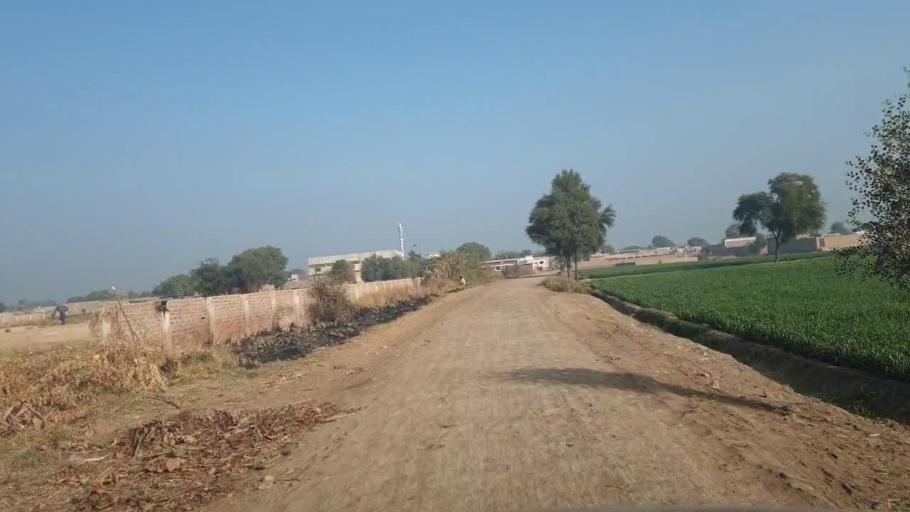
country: PK
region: Sindh
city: Shahdadpur
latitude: 25.9382
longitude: 68.6063
